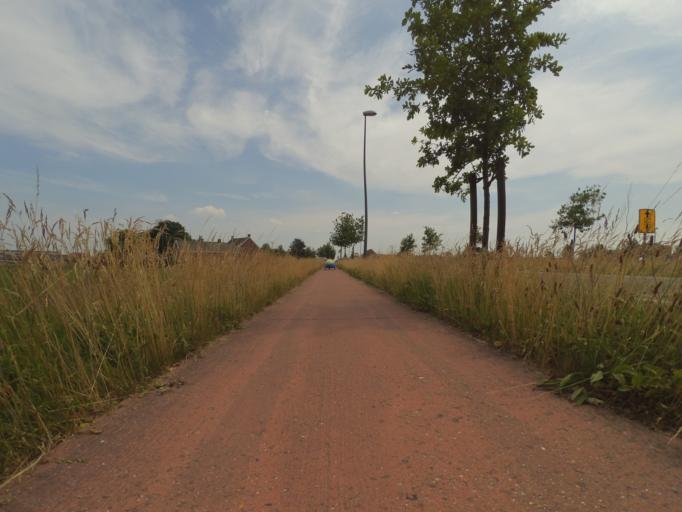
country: BE
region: Flanders
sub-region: Provincie Antwerpen
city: Brecht
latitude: 51.4047
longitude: 4.6666
